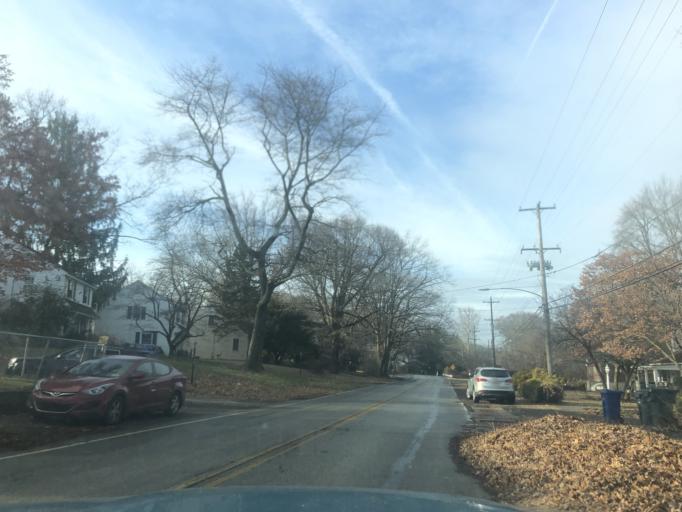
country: US
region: Pennsylvania
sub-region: Montgomery County
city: Jenkintown
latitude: 40.1212
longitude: -75.1305
